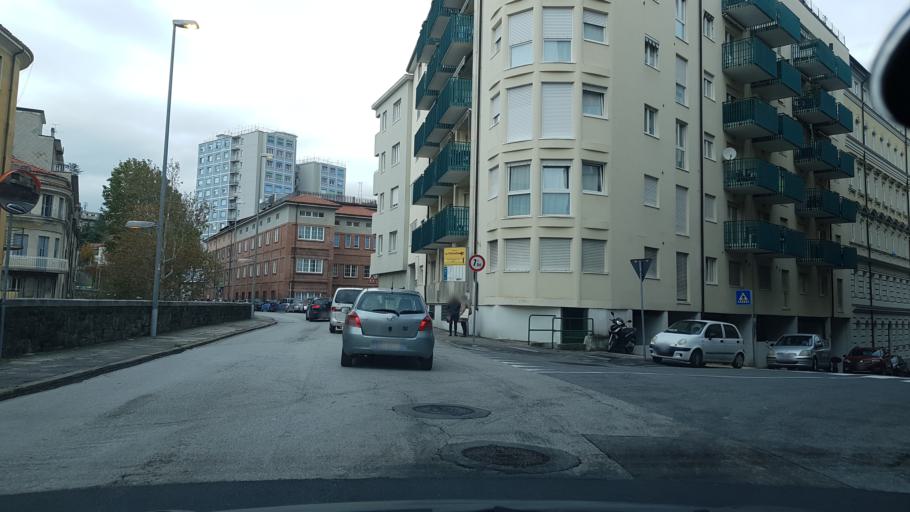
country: IT
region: Friuli Venezia Giulia
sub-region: Provincia di Trieste
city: Trieste
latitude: 45.6635
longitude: 13.7707
